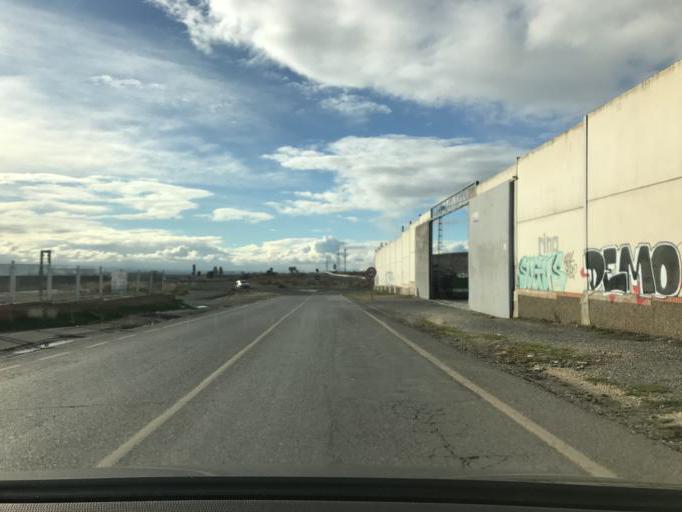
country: ES
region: Andalusia
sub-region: Provincia de Granada
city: Albolote
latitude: 37.2271
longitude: -3.6646
